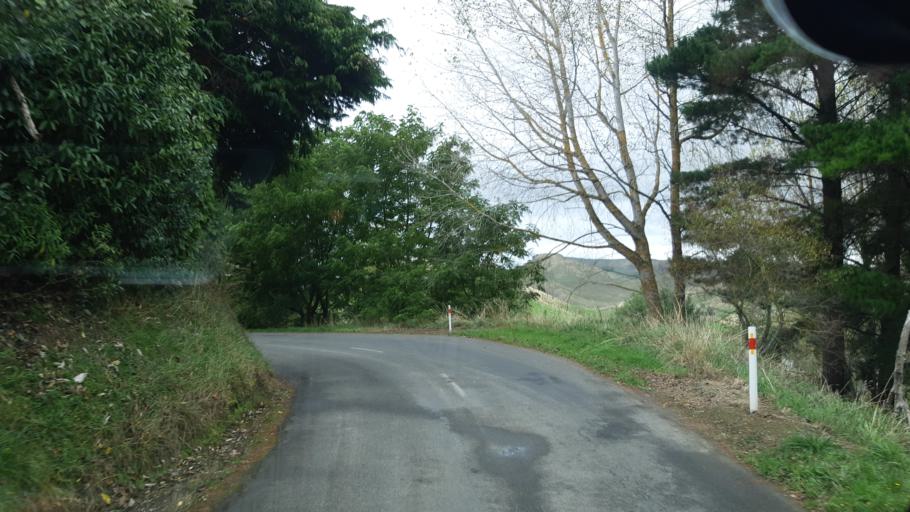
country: NZ
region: Manawatu-Wanganui
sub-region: Ruapehu District
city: Waiouru
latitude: -39.6117
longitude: 175.6608
